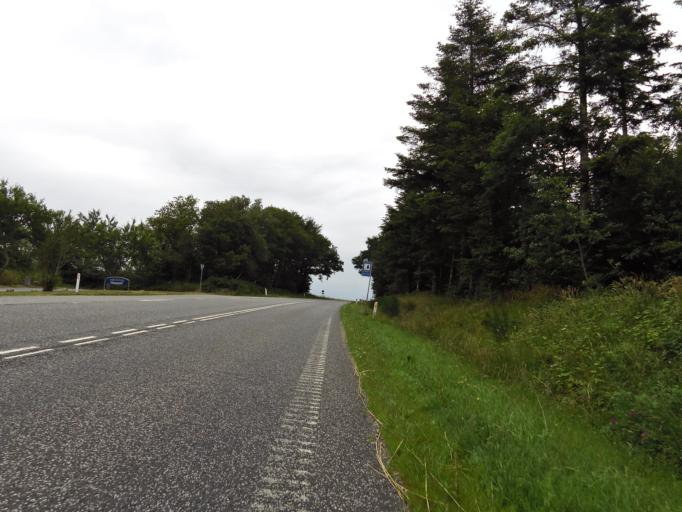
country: DK
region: South Denmark
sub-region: Tonder Kommune
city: Logumkloster
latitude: 55.1204
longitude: 8.9626
